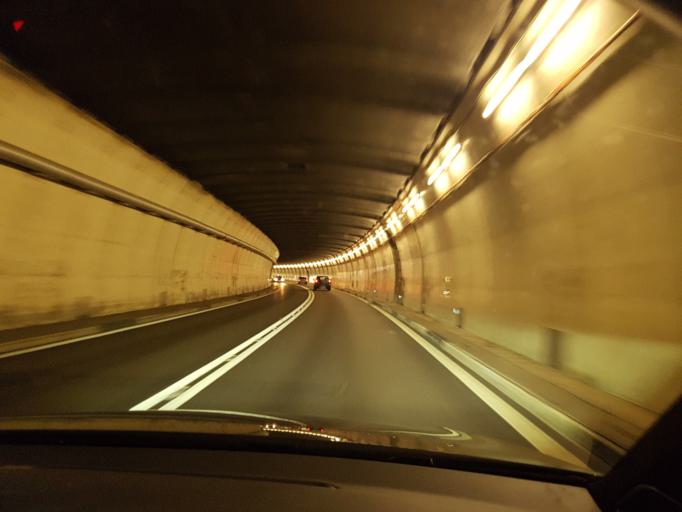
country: CH
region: Schwyz
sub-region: Bezirk Schwyz
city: Ingenbohl
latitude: 46.9960
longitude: 8.6171
